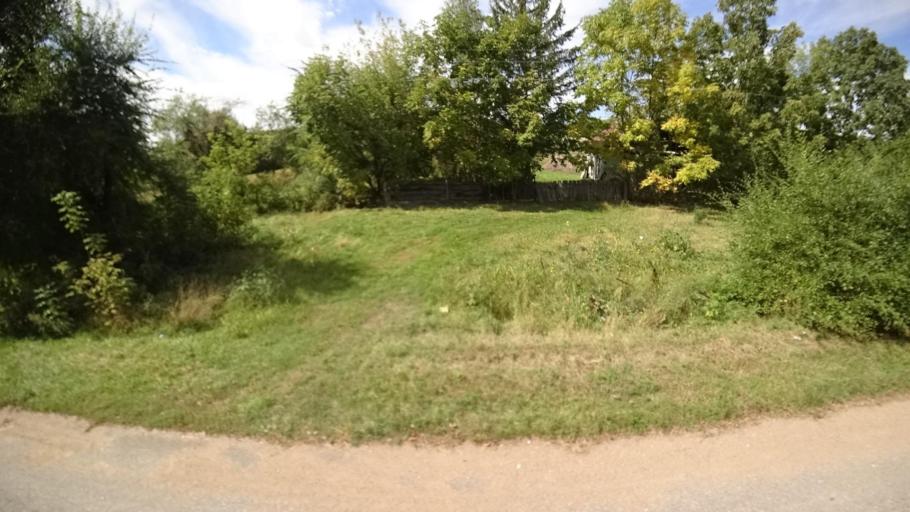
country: RU
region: Primorskiy
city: Yakovlevka
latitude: 44.6473
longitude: 133.5967
